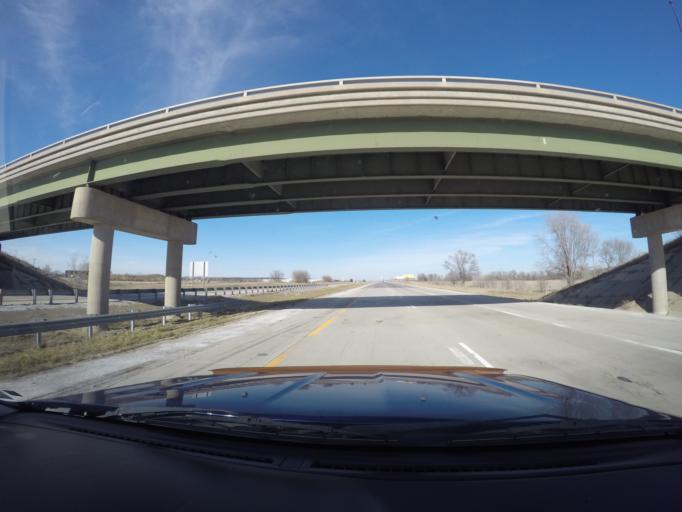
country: US
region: Kansas
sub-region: Sedgwick County
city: Park City
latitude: 37.8105
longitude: -97.3263
